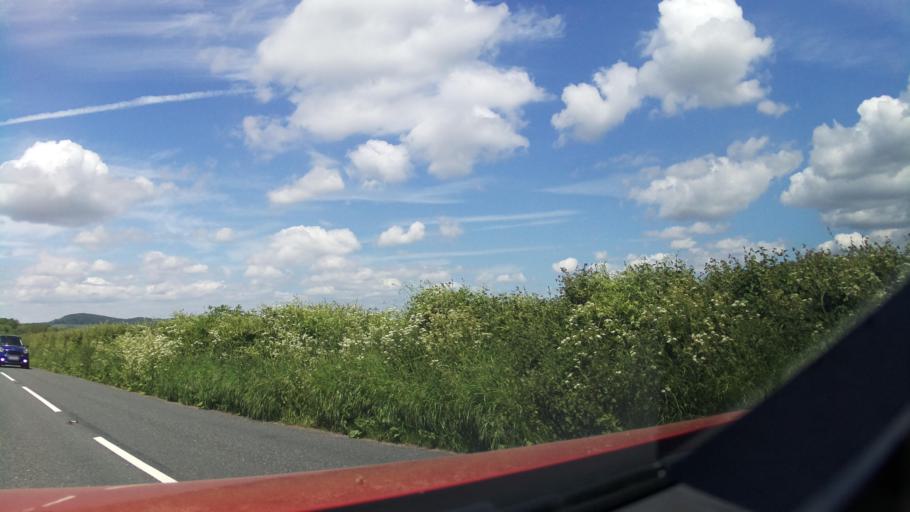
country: GB
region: Wales
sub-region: Monmouthshire
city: Monmouth
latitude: 51.7941
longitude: -2.7170
